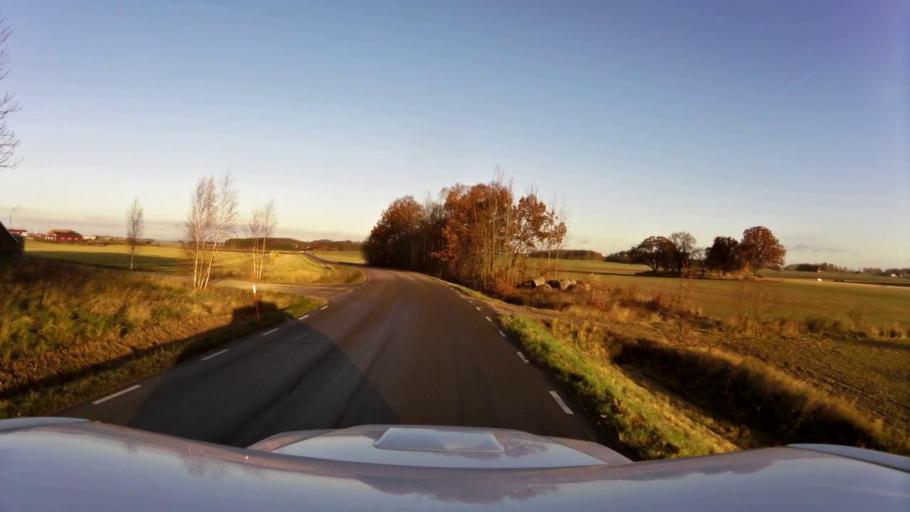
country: SE
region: OEstergoetland
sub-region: Linkopings Kommun
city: Ekangen
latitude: 58.4362
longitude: 15.6807
